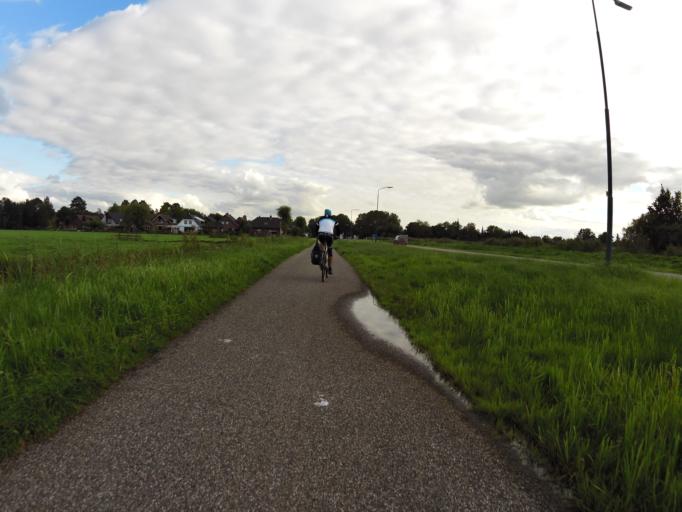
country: NL
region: Utrecht
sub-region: Stichtse Vecht
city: Breukelen
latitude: 52.1538
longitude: 4.9464
